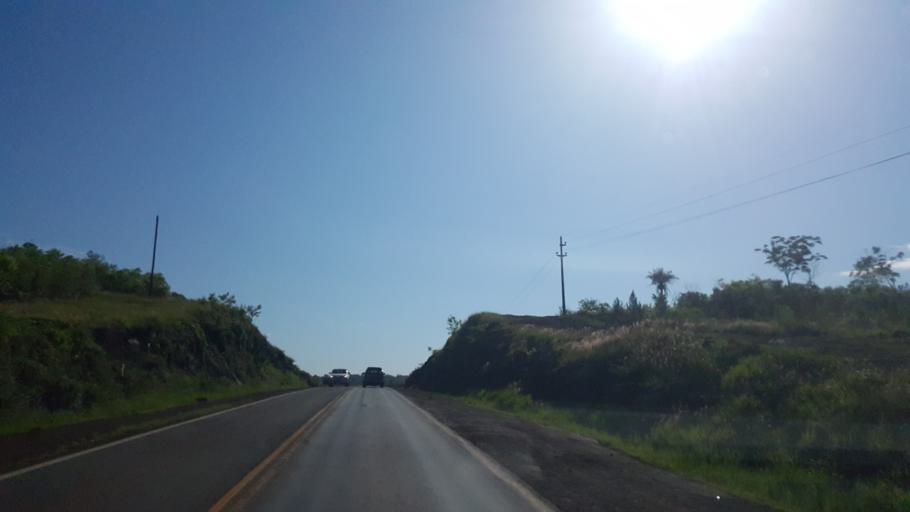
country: AR
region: Misiones
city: Santa Ana
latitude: -27.3714
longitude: -55.5667
